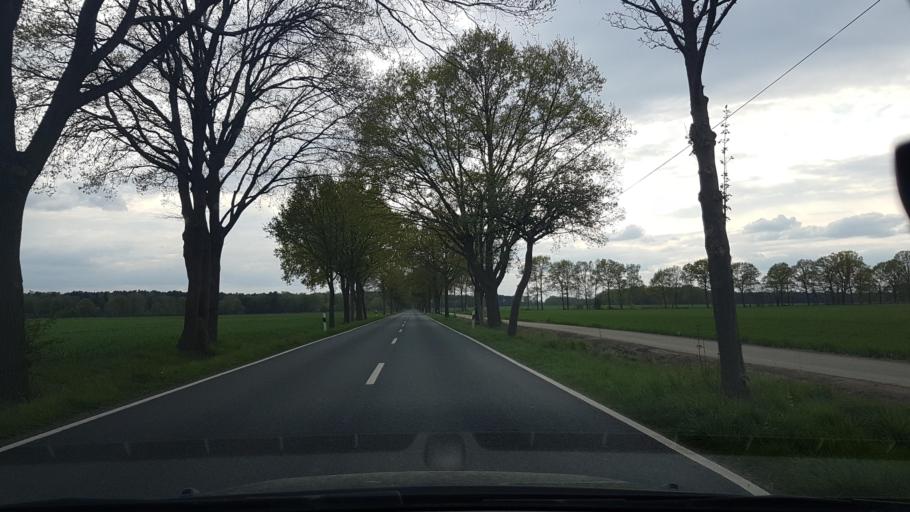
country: DE
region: Lower Saxony
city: Elze
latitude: 52.5185
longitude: 9.6936
